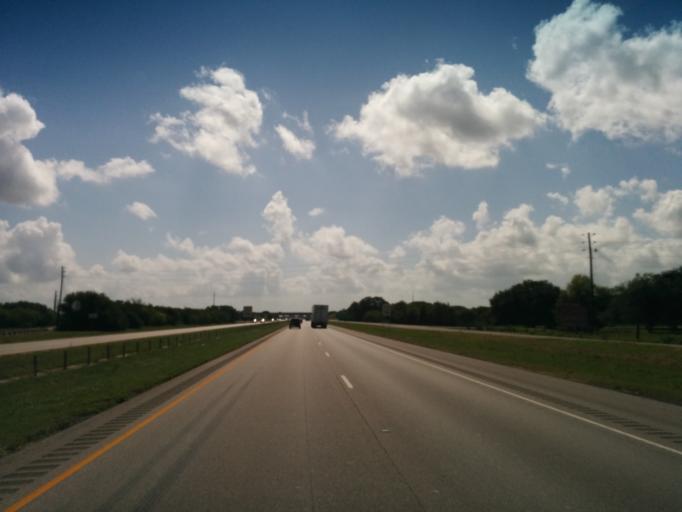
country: US
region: Texas
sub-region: Colorado County
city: Columbus
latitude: 29.6935
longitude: -96.5804
